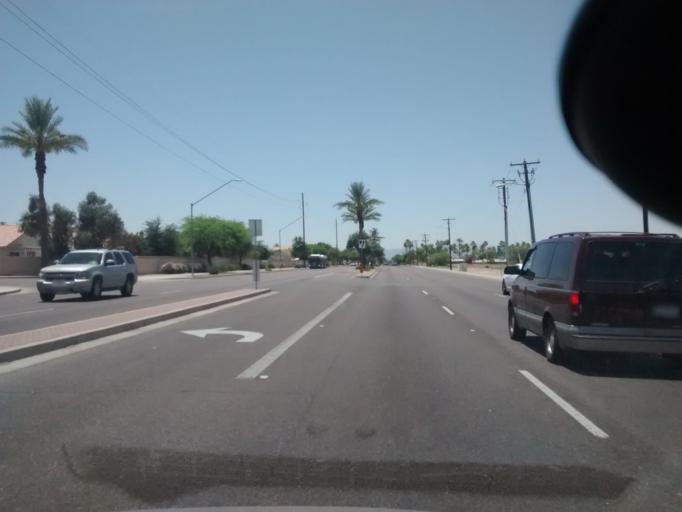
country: US
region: Arizona
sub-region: Maricopa County
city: Glendale
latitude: 33.5379
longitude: -112.2253
